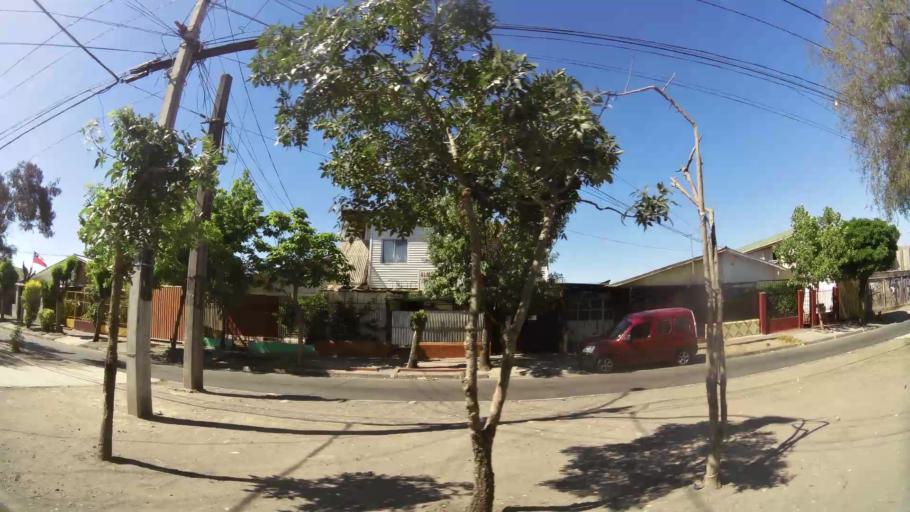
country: CL
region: Santiago Metropolitan
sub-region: Provincia de Maipo
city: San Bernardo
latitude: -33.5846
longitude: -70.6804
